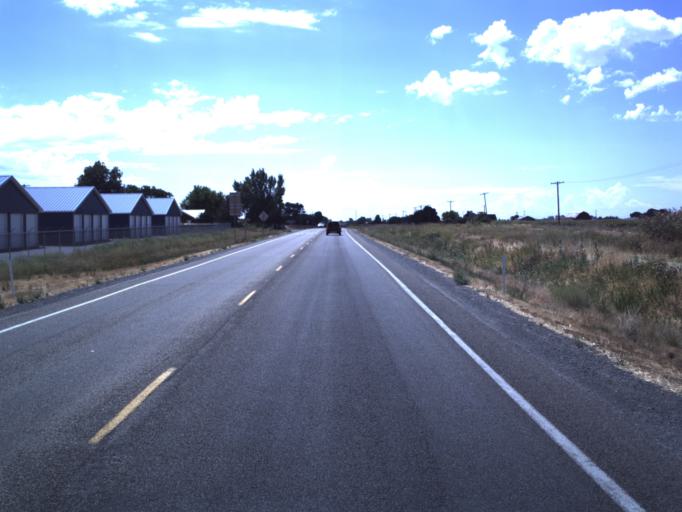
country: US
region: Utah
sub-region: Box Elder County
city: Elwood
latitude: 41.7090
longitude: -112.1422
